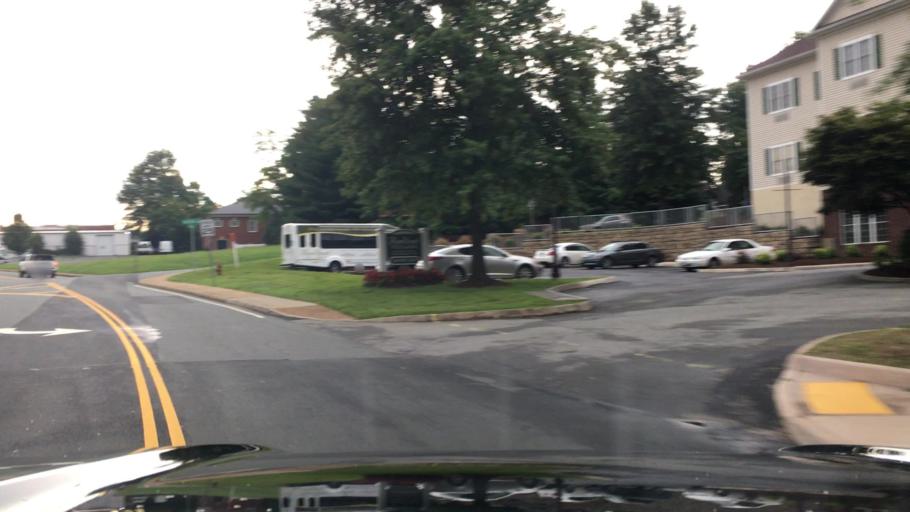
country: US
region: Virginia
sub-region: City of Charlottesville
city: Charlottesville
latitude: 38.0692
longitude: -78.4813
